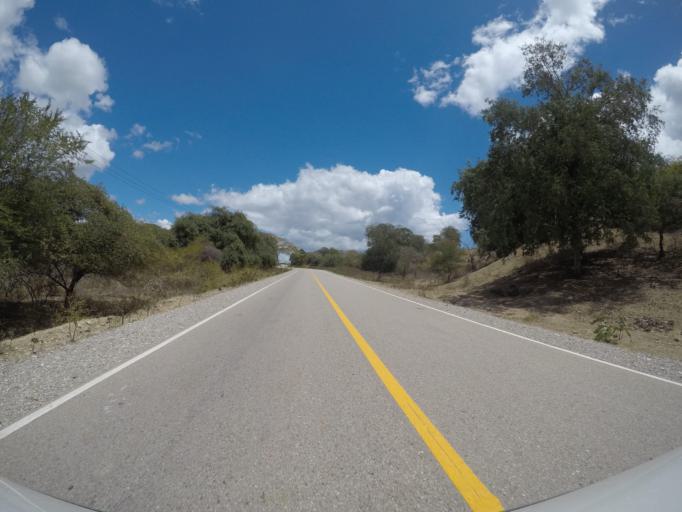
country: TL
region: Lautem
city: Lospalos
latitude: -8.4034
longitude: 126.8254
